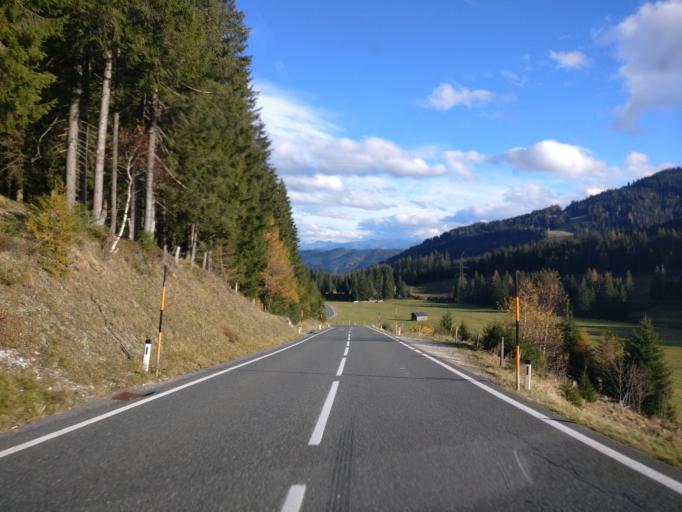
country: AT
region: Salzburg
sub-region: Politischer Bezirk Zell am See
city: Dienten am Hochkonig
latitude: 47.3916
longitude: 13.0596
